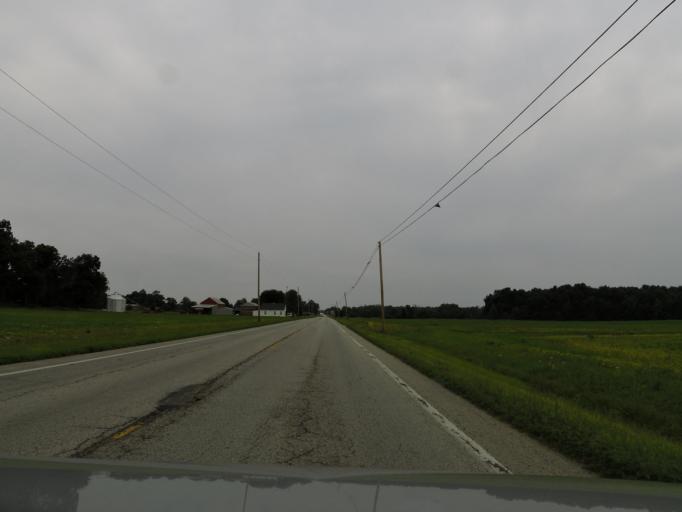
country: US
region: Ohio
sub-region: Brown County
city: Mount Orab
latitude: 39.1277
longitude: -83.9333
